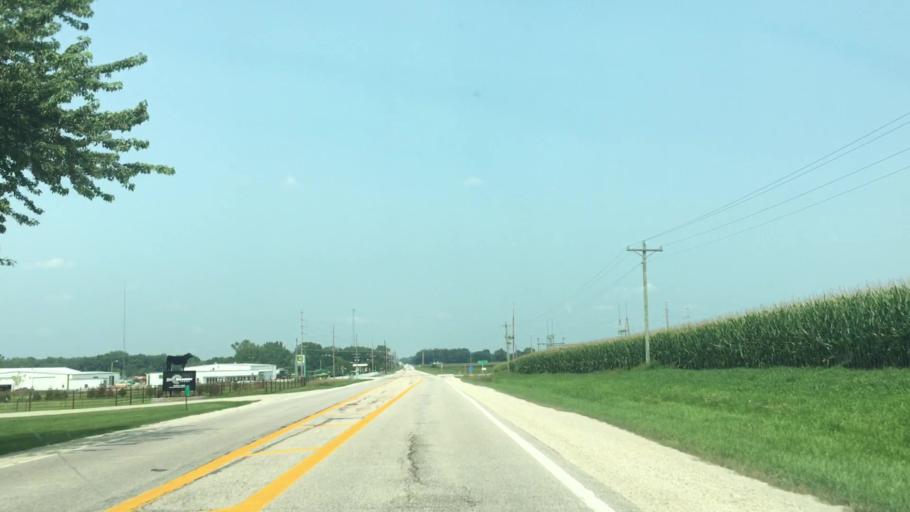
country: US
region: Iowa
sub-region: Buchanan County
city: Independence
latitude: 42.3683
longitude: -91.8893
